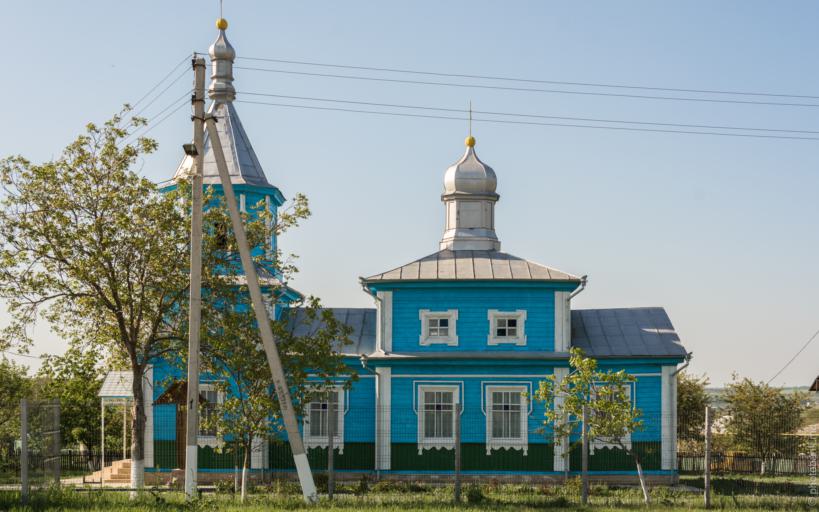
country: MD
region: Balti
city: Balti
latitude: 47.7071
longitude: 27.8696
